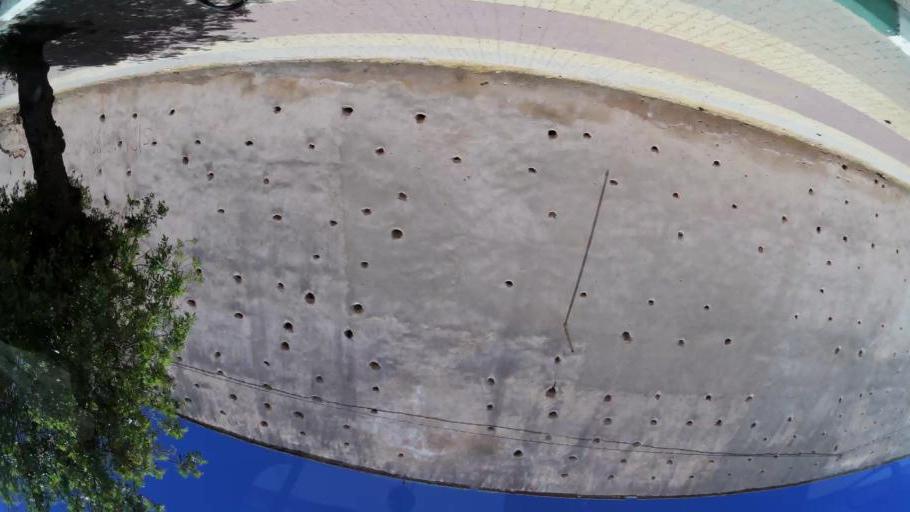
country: MA
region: Meknes-Tafilalet
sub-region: Meknes
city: Meknes
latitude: 33.9057
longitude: -5.5739
